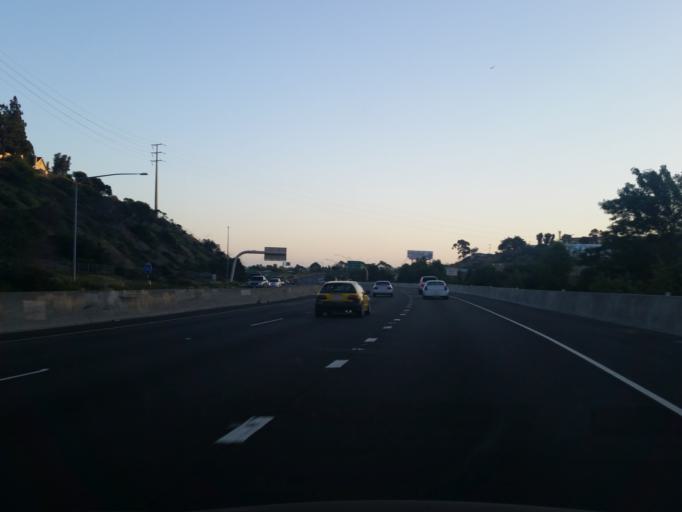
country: US
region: California
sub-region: San Diego County
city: San Diego
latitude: 32.7219
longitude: -117.1166
